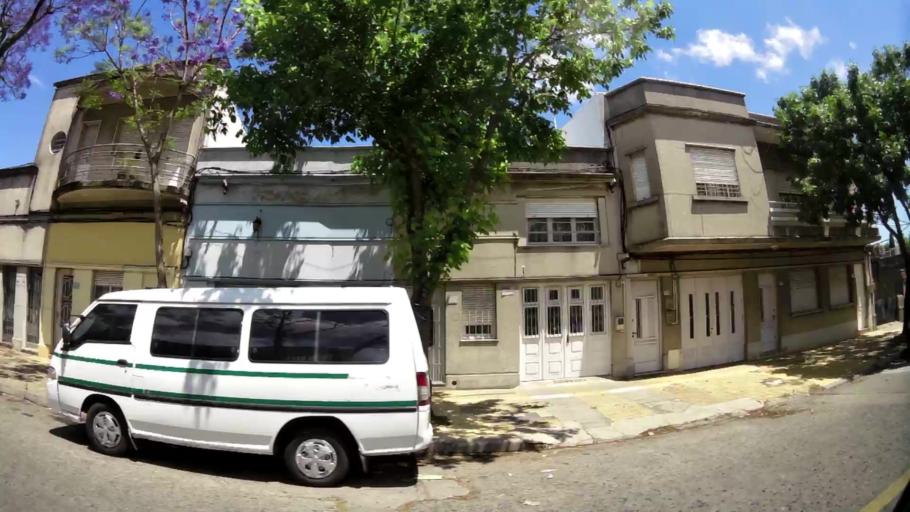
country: UY
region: Montevideo
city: Montevideo
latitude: -34.8710
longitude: -56.1990
